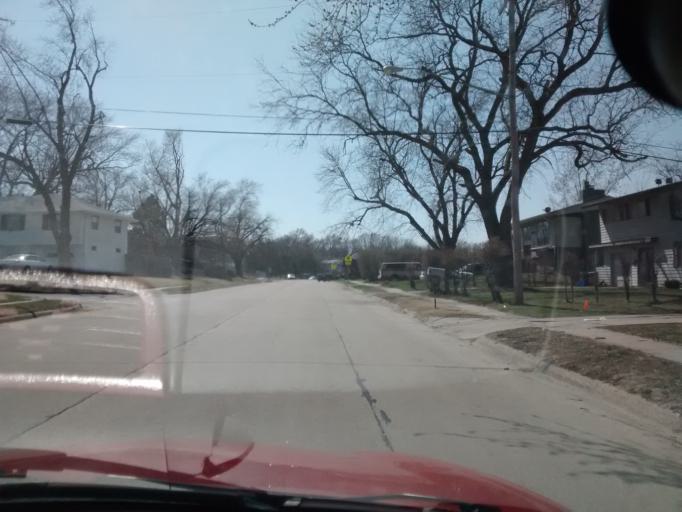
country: US
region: Nebraska
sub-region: Sarpy County
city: Bellevue
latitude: 41.1504
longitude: -95.9135
